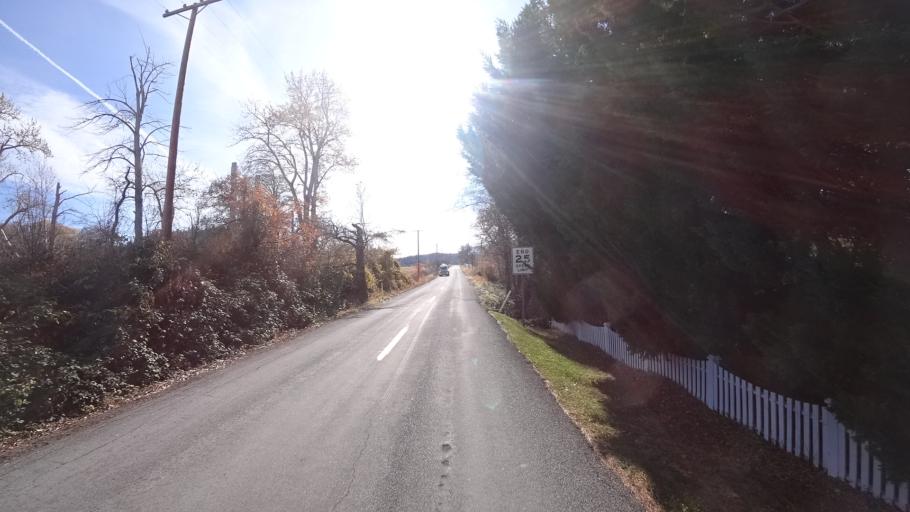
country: US
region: California
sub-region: Siskiyou County
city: Weed
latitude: 41.4555
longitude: -122.4316
